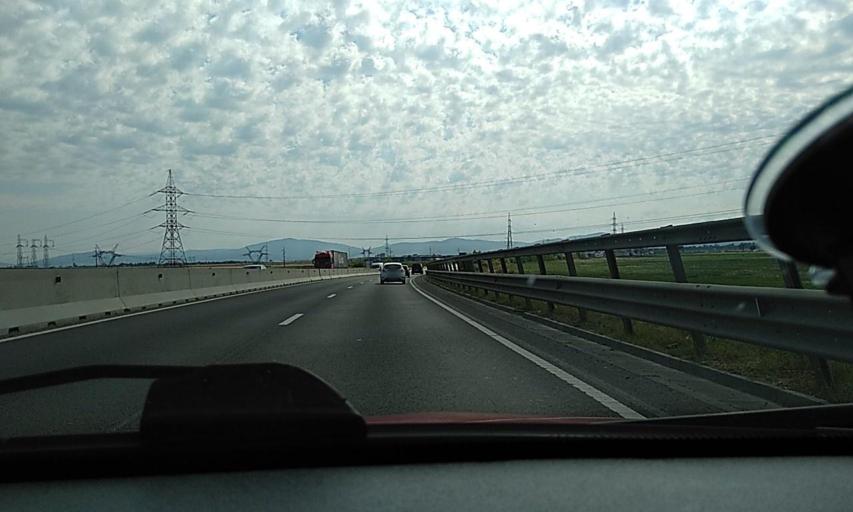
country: RO
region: Brasov
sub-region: Comuna Sanpetru
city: Sanpetru
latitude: 45.6843
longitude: 25.6469
